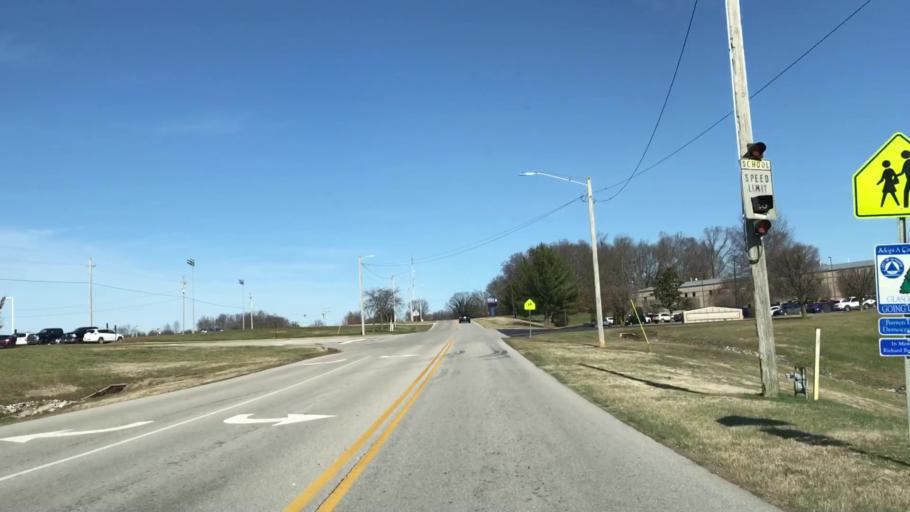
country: US
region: Kentucky
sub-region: Barren County
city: Glasgow
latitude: 37.0089
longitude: -85.8863
